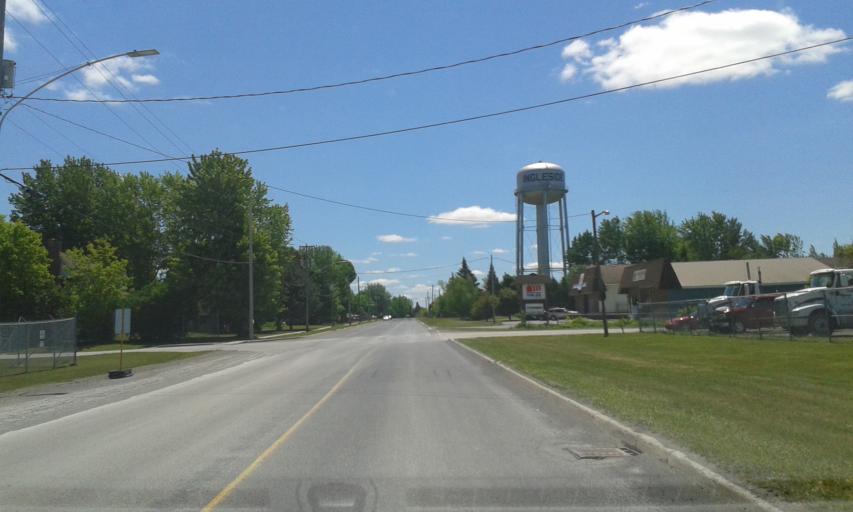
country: US
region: New York
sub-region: St. Lawrence County
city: Massena
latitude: 45.0033
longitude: -74.9922
